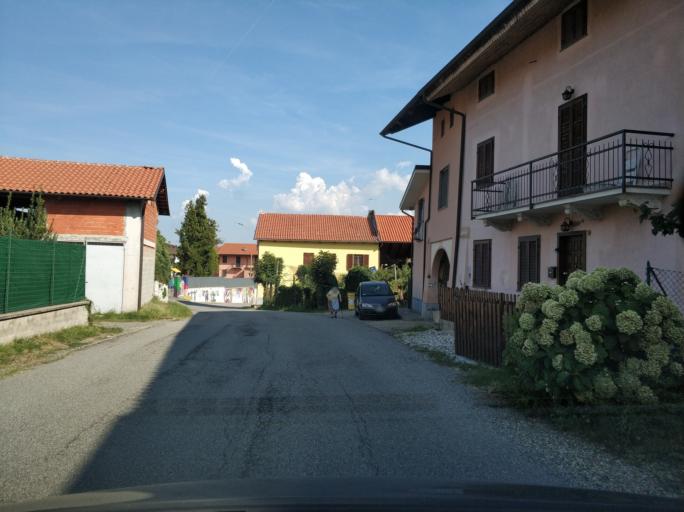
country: IT
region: Piedmont
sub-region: Provincia di Torino
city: Nole
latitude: 45.2570
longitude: 7.5783
